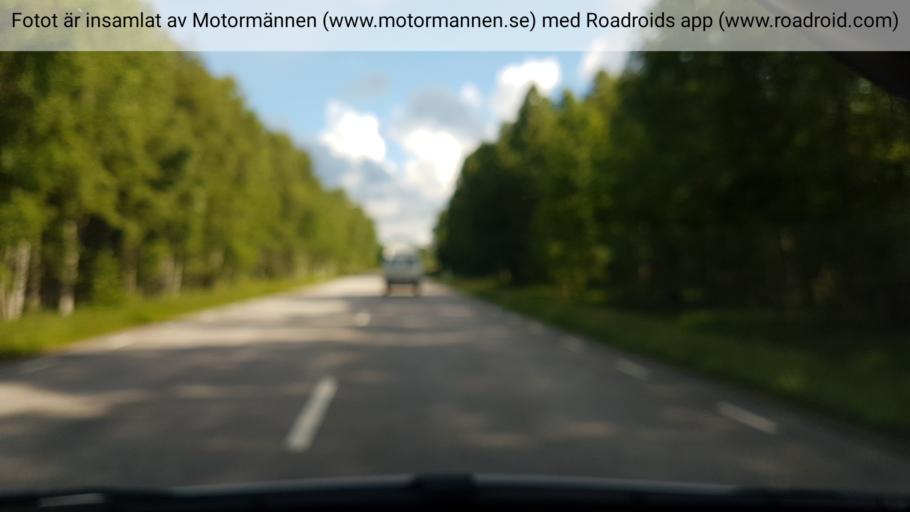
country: SE
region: Vaestra Goetaland
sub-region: Karlsborgs Kommun
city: Karlsborg
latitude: 58.5822
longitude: 14.5001
